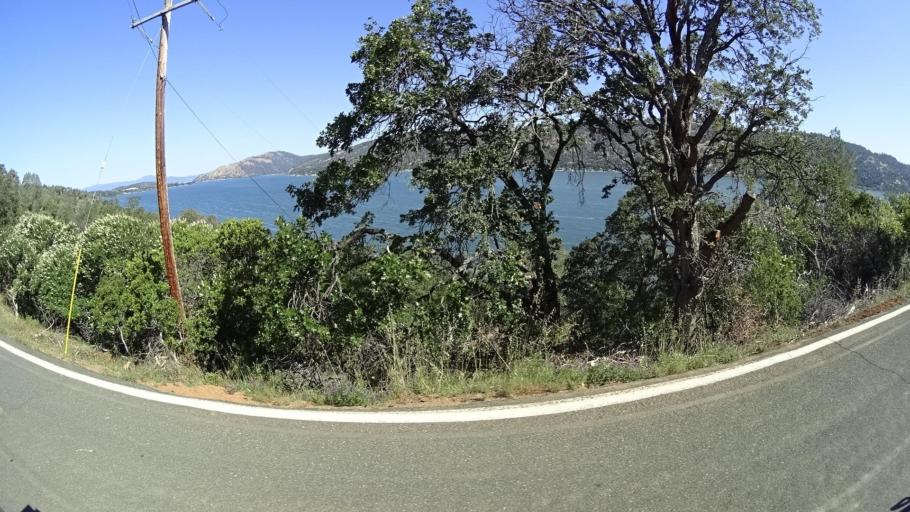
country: US
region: California
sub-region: Lake County
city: Clearlake Oaks
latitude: 39.0043
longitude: -122.7119
